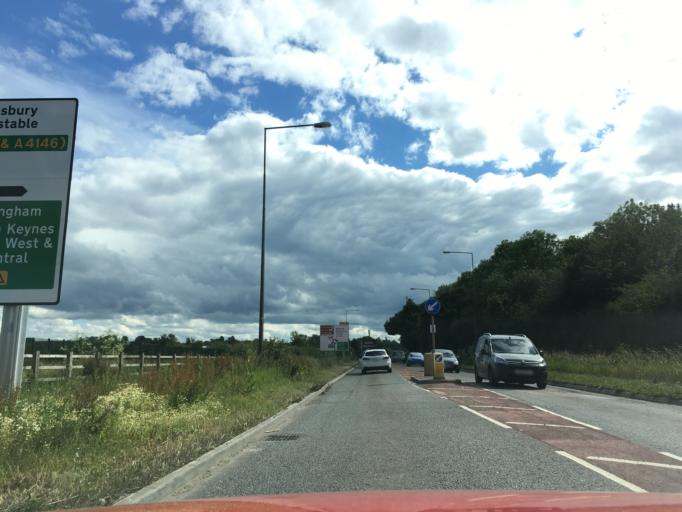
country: GB
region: England
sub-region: Milton Keynes
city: Wavendon
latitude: 52.0359
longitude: -0.6767
